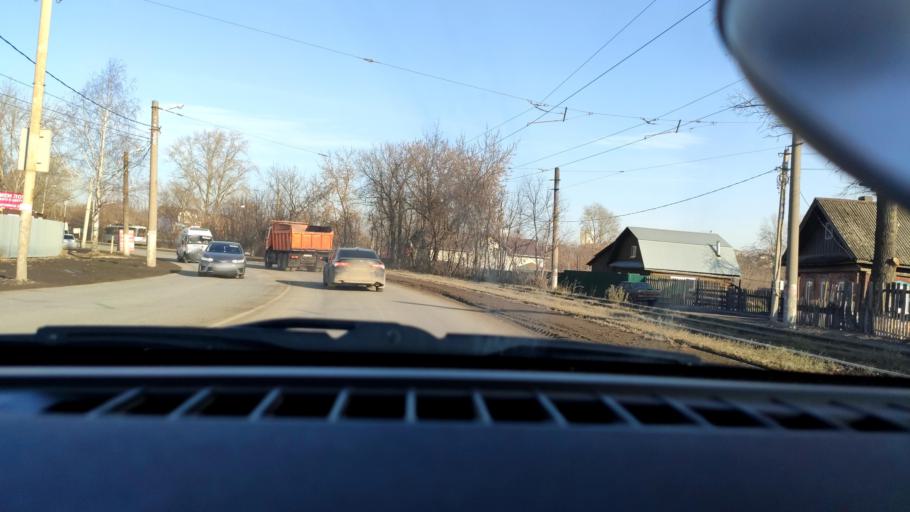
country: RU
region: Perm
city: Kondratovo
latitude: 57.9544
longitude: 56.1347
